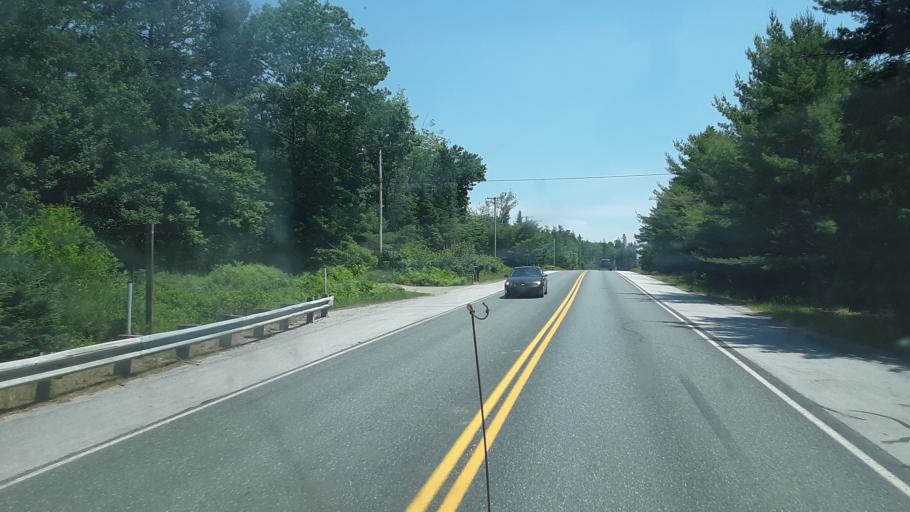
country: US
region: Maine
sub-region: Hancock County
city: Hancock
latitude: 44.5332
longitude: -68.2681
